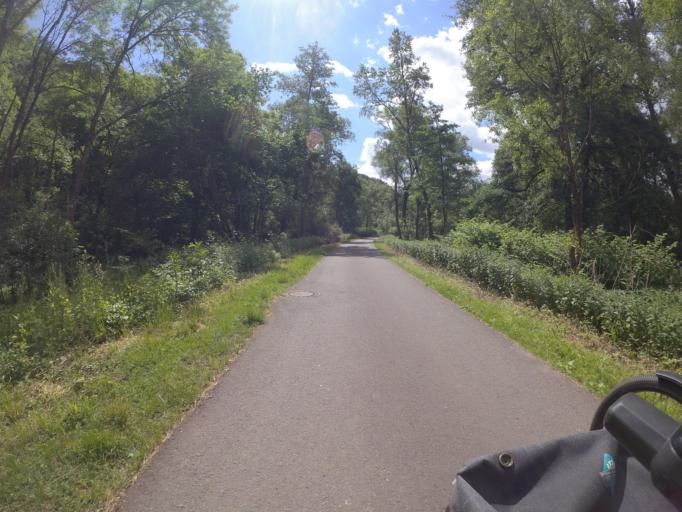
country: DE
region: Rheinland-Pfalz
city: Boos
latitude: 49.7835
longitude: 7.7106
